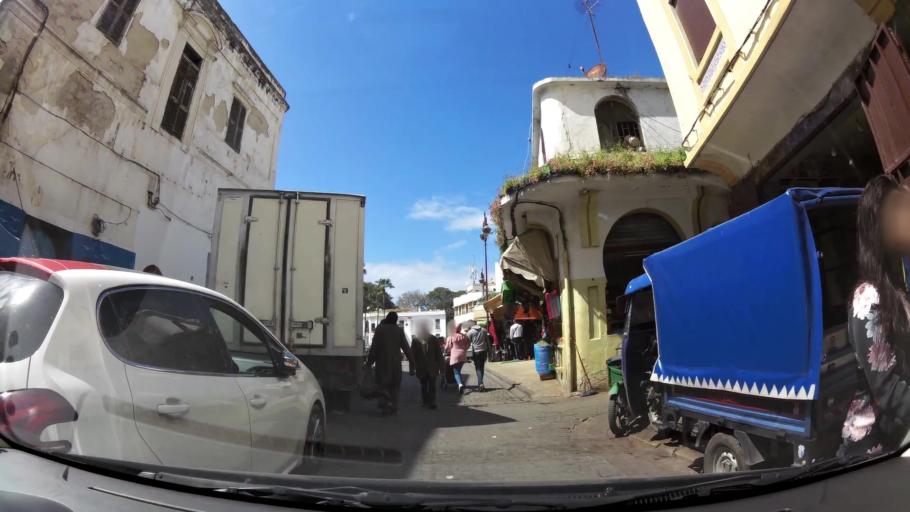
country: MA
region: Tanger-Tetouan
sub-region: Tanger-Assilah
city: Tangier
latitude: 35.7842
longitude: -5.8121
